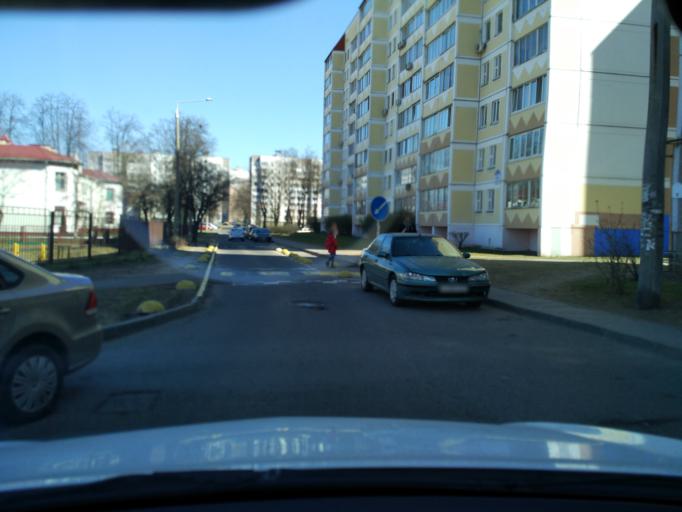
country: BY
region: Minsk
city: Minsk
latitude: 53.8791
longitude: 27.5528
